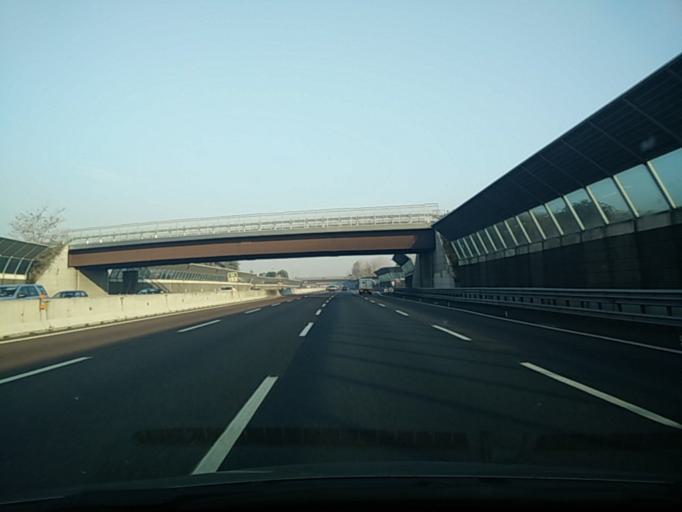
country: IT
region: Lombardy
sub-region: Citta metropolitana di Milano
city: Trezzo sull'Adda
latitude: 45.6006
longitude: 9.5160
